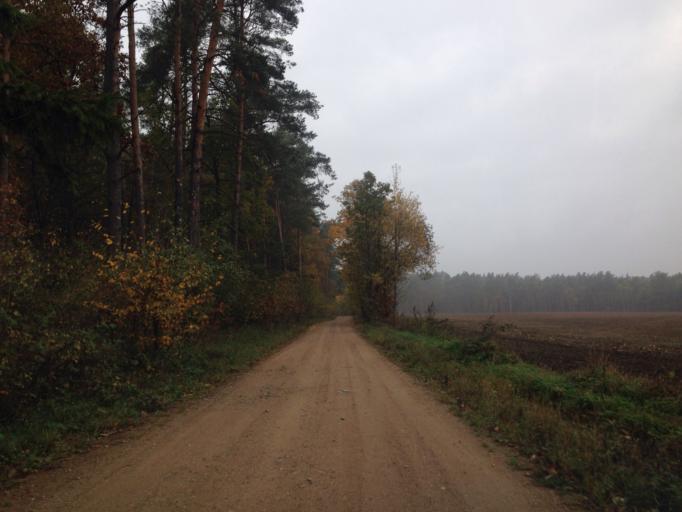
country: PL
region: Warmian-Masurian Voivodeship
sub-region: Powiat dzialdowski
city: Lidzbark
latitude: 53.2639
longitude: 19.7452
